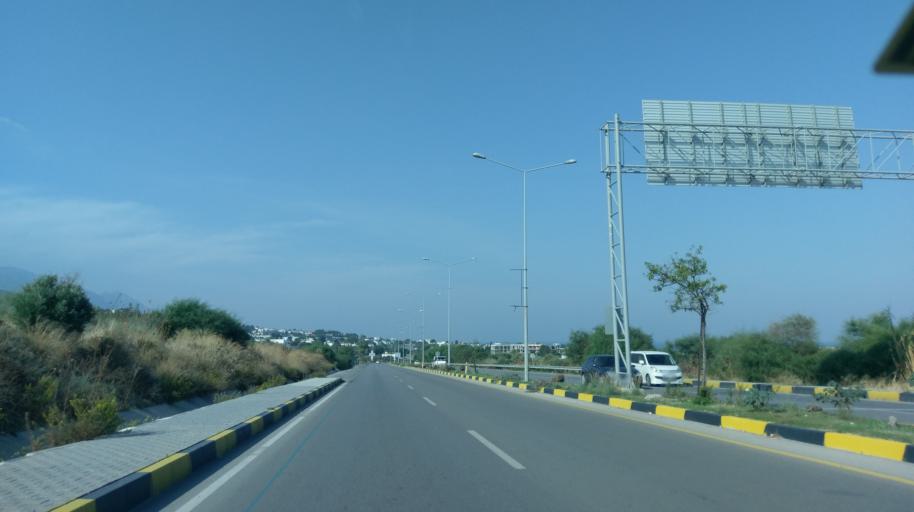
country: CY
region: Keryneia
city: Kyrenia
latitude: 35.3315
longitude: 33.2732
